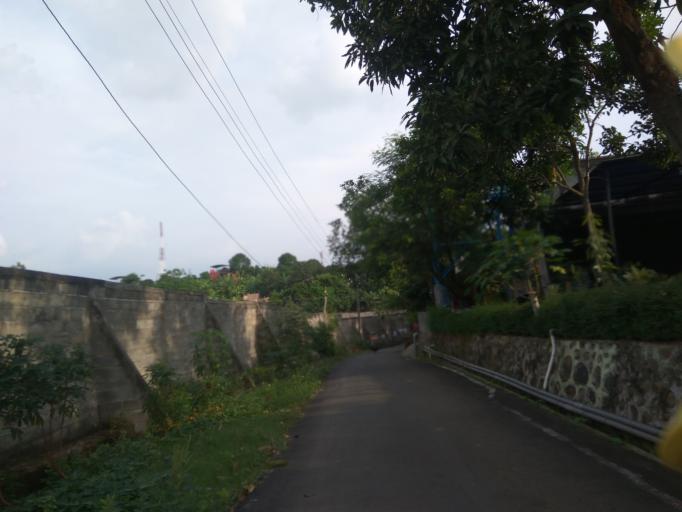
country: ID
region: Central Java
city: Semarang
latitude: -7.0292
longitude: 110.4422
